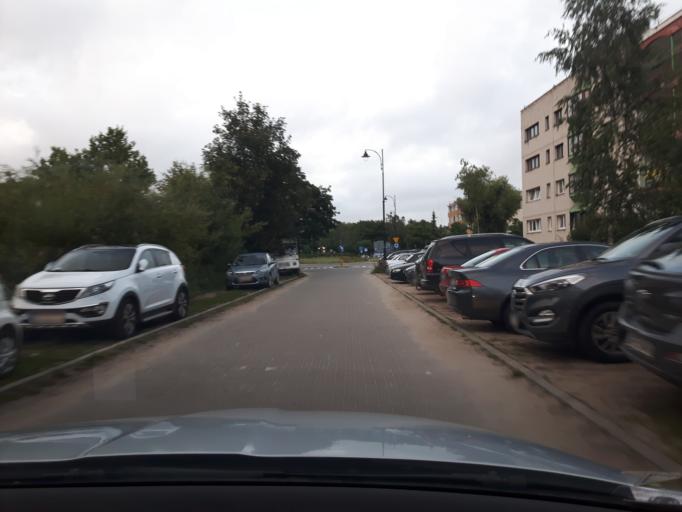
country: PL
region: Pomeranian Voivodeship
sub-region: Sopot
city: Sopot
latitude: 54.4320
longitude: 18.5814
